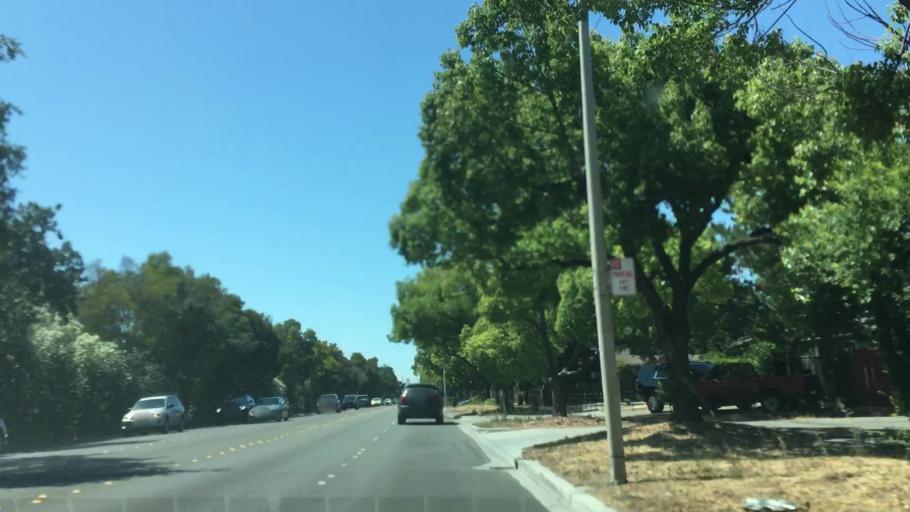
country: US
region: California
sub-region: Santa Clara County
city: Palo Alto
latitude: 37.4211
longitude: -122.1283
